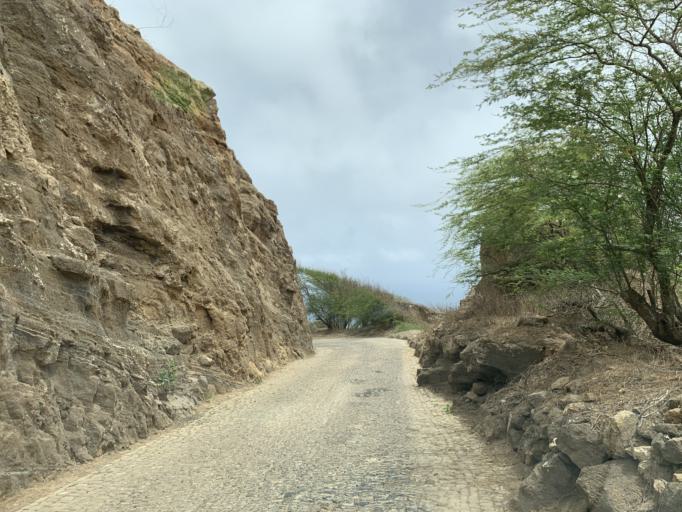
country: CV
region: Brava
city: Vila Nova Sintra
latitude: 14.8753
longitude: -24.7248
